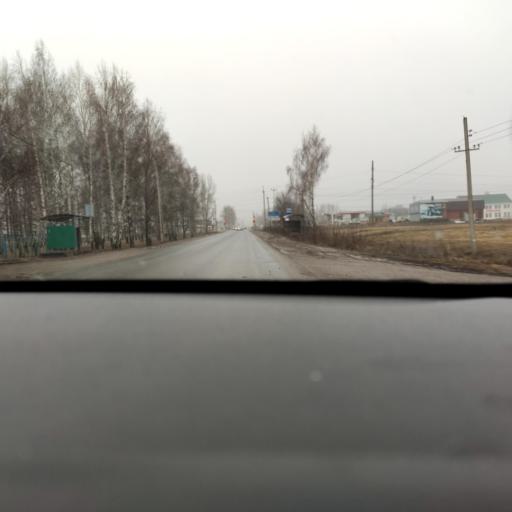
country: RU
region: Tatarstan
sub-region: Chistopol'skiy Rayon
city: Chistopol'
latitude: 55.3519
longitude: 50.6687
